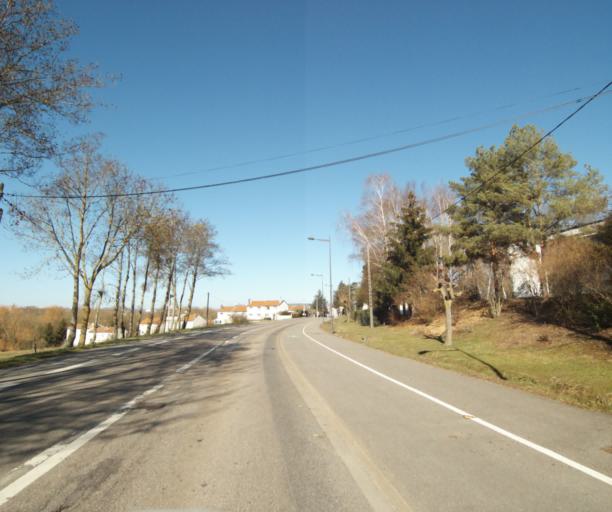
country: FR
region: Lorraine
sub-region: Departement de Meurthe-et-Moselle
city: Heillecourt
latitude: 48.6575
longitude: 6.2064
